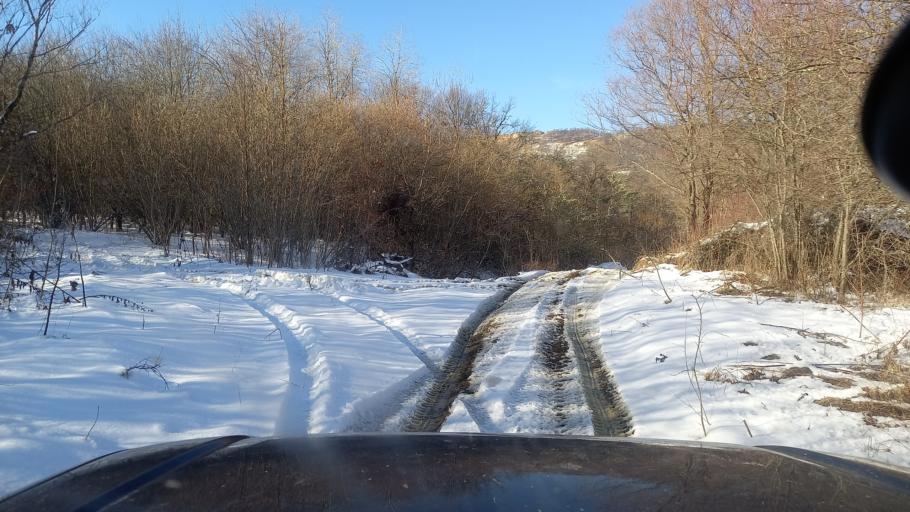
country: RU
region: Adygeya
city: Kamennomostskiy
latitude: 44.2129
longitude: 40.1399
